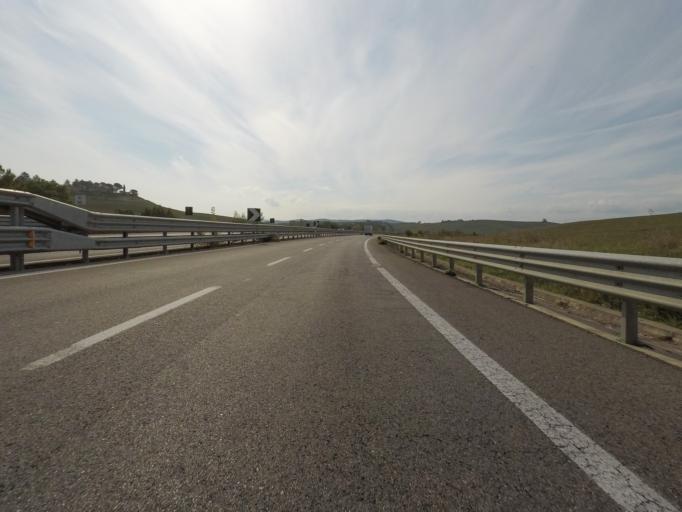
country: IT
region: Tuscany
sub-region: Provincia di Siena
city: Isola D'Arbia
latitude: 43.2613
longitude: 11.3280
